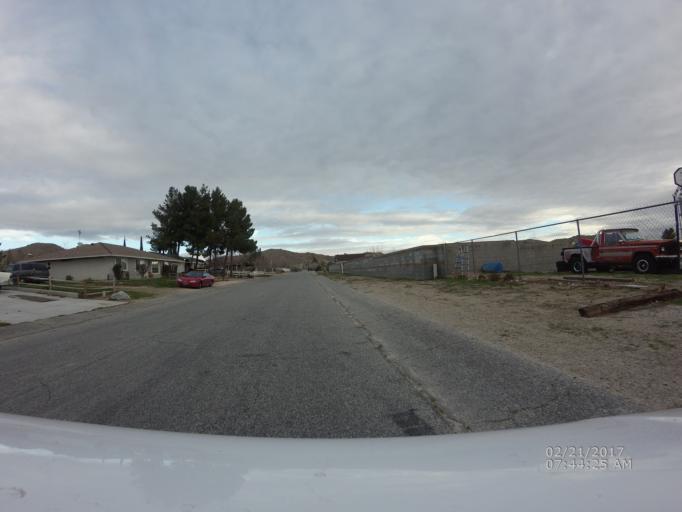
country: US
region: California
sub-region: Los Angeles County
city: Lake Los Angeles
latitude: 34.5960
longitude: -117.8436
